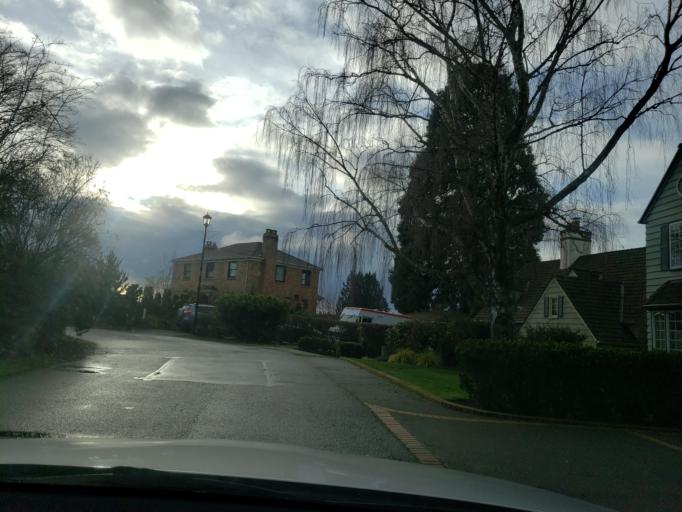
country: US
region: Washington
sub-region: King County
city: Shoreline
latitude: 47.7021
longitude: -122.3808
